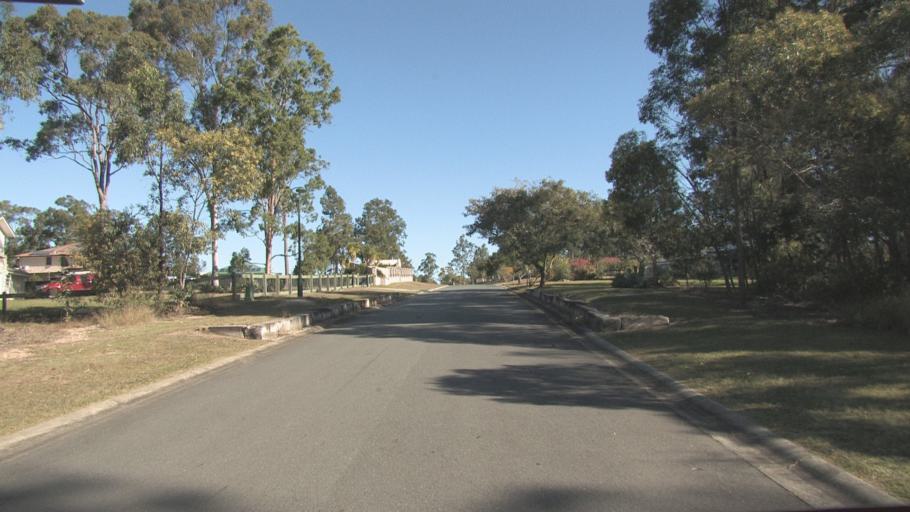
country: AU
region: Queensland
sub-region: Ipswich
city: Springfield Lakes
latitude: -27.7254
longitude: 152.9236
